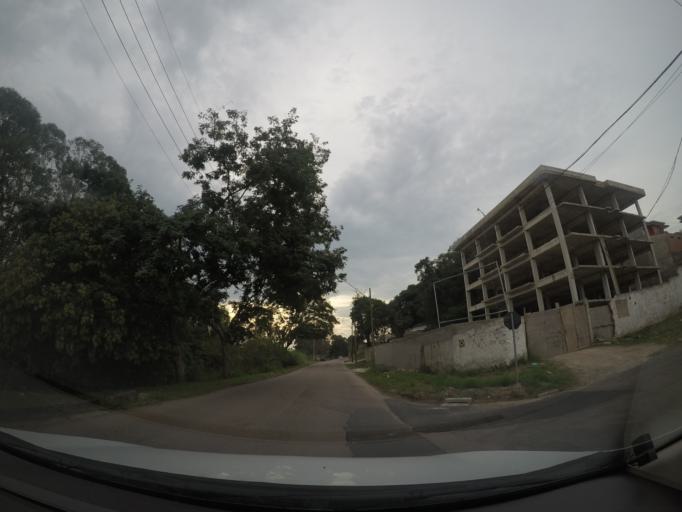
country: BR
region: Parana
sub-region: Curitiba
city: Curitiba
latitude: -25.4677
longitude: -49.2486
